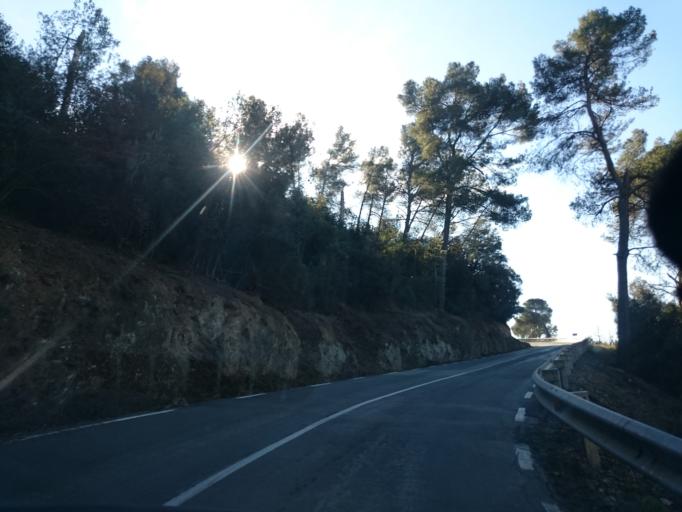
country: ES
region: Catalonia
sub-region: Provincia de Barcelona
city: Molins de Rei
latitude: 41.4279
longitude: 2.0462
